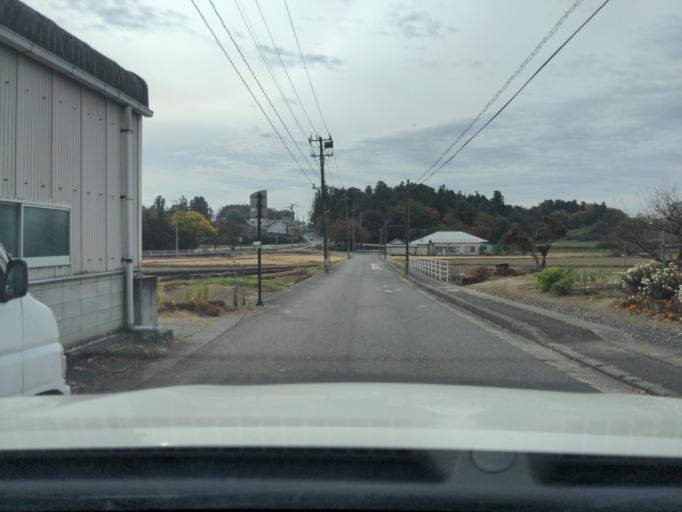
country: JP
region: Fukushima
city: Koriyama
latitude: 37.3624
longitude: 140.2885
